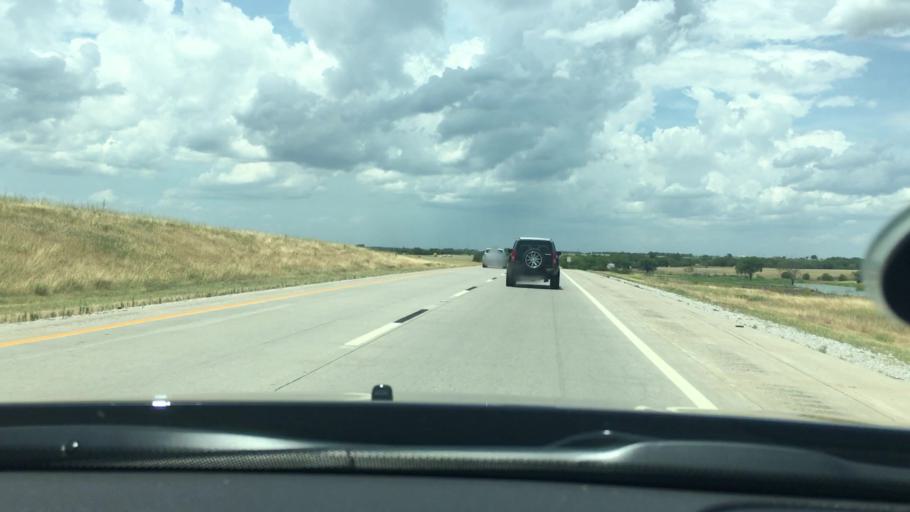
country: US
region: Oklahoma
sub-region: Carter County
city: Ardmore
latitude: 34.0851
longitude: -97.1498
